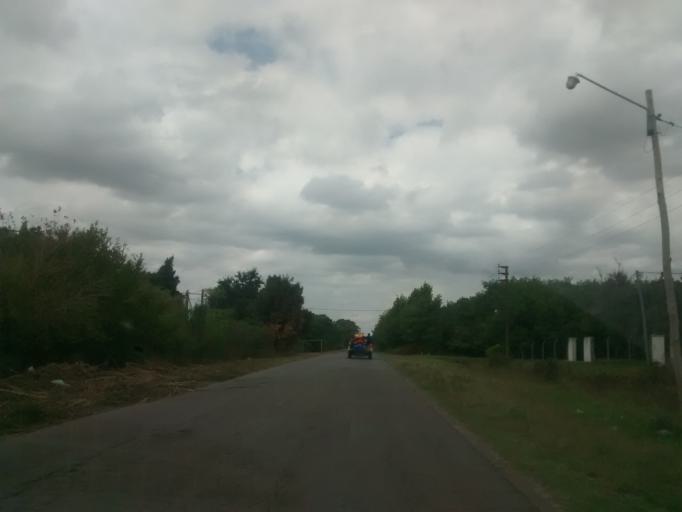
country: AR
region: Buenos Aires
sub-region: Partido de La Plata
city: La Plata
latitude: -34.9773
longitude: -57.9352
